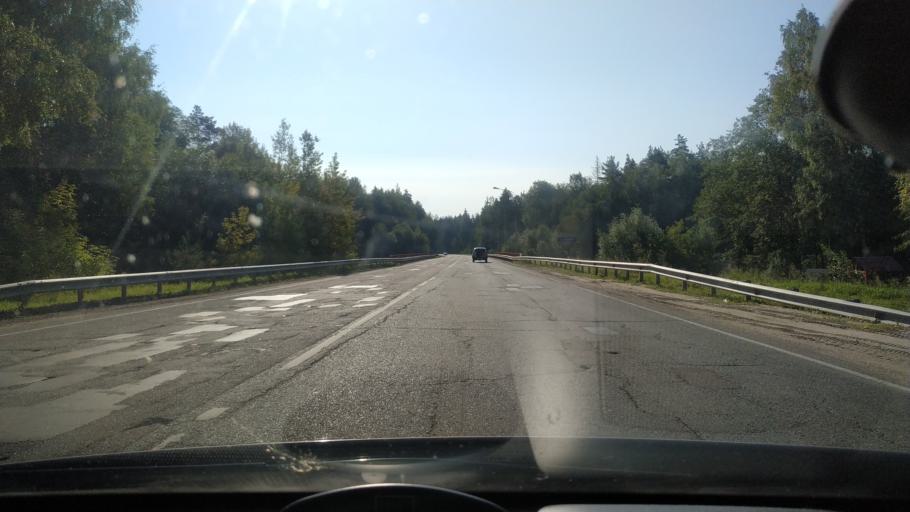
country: RU
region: Moskovskaya
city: Kerva
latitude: 55.5657
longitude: 39.6517
